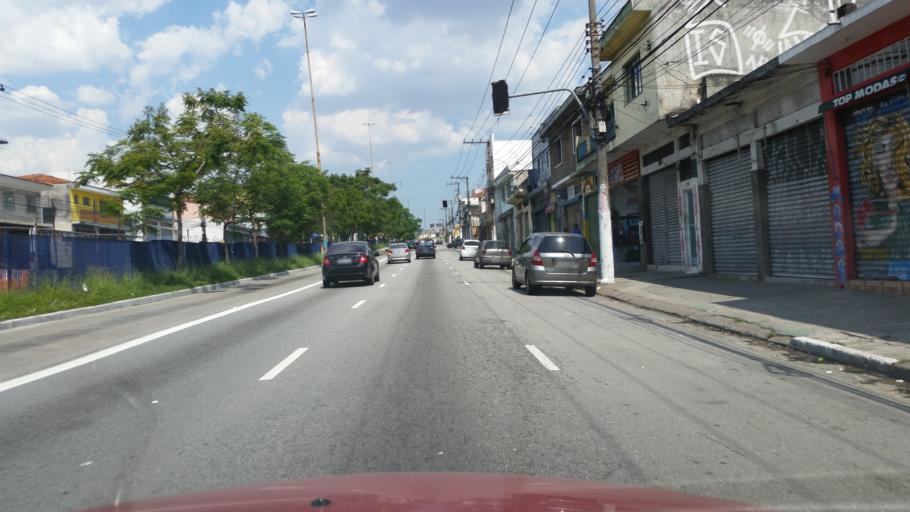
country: BR
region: Sao Paulo
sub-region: Diadema
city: Diadema
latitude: -23.6681
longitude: -46.6521
